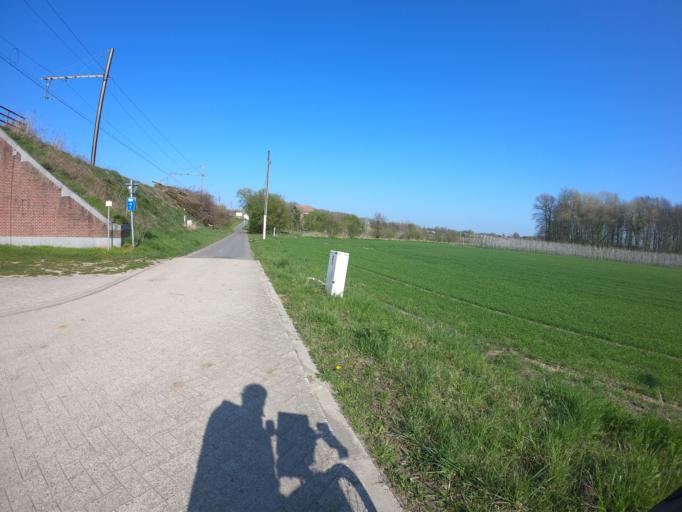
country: BE
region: Flanders
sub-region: Provincie Limburg
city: Sint-Truiden
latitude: 50.8277
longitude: 5.1891
